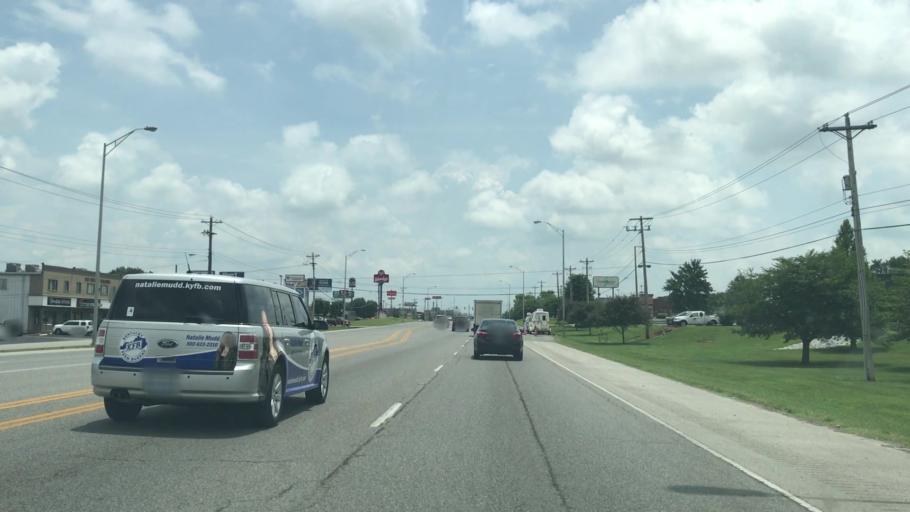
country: US
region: Kentucky
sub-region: Warren County
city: Bowling Green
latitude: 36.9523
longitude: -86.4260
